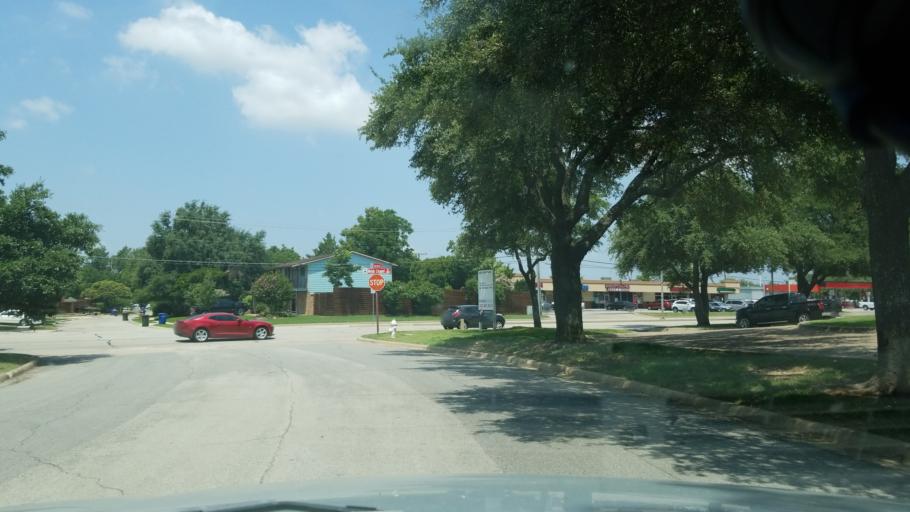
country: US
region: Texas
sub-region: Dallas County
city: Carrollton
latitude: 32.9519
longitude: -96.8704
